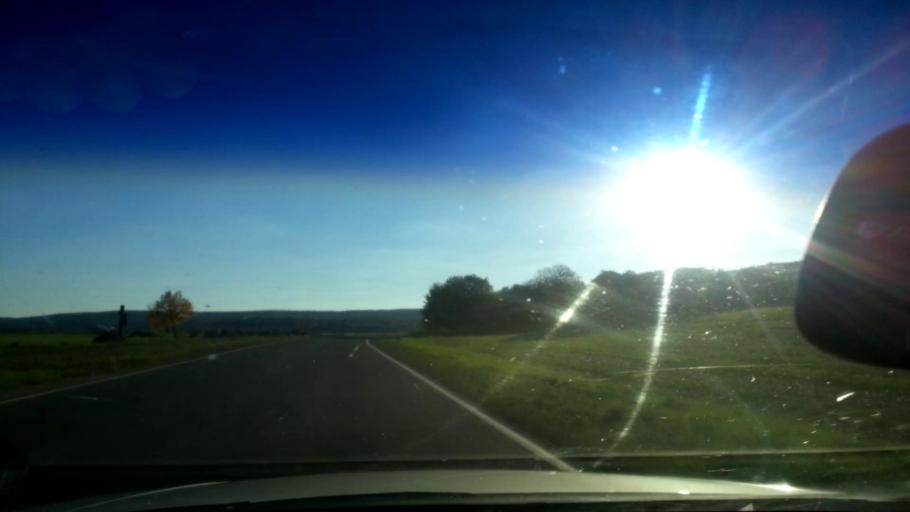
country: DE
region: Bavaria
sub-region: Upper Franconia
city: Baunach
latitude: 49.9978
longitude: 10.8698
